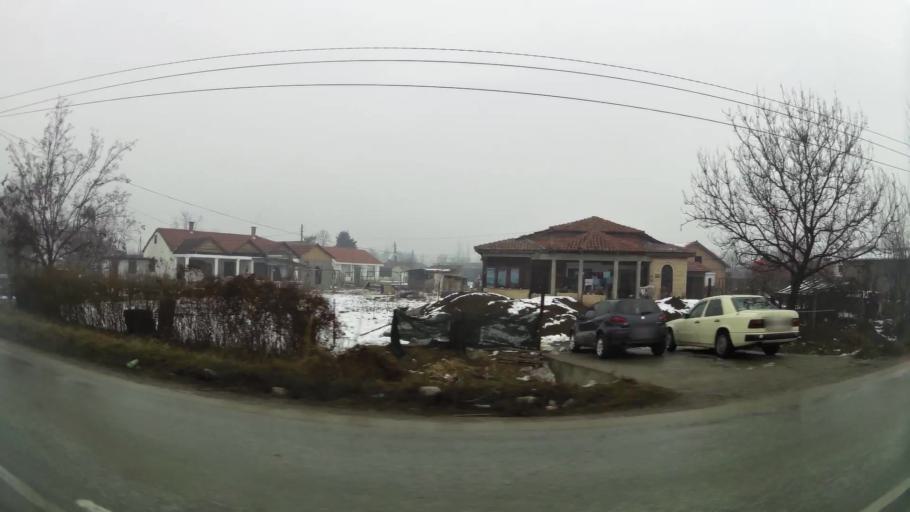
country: MK
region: Ilinden
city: Idrizovo
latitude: 41.9496
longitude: 21.5881
